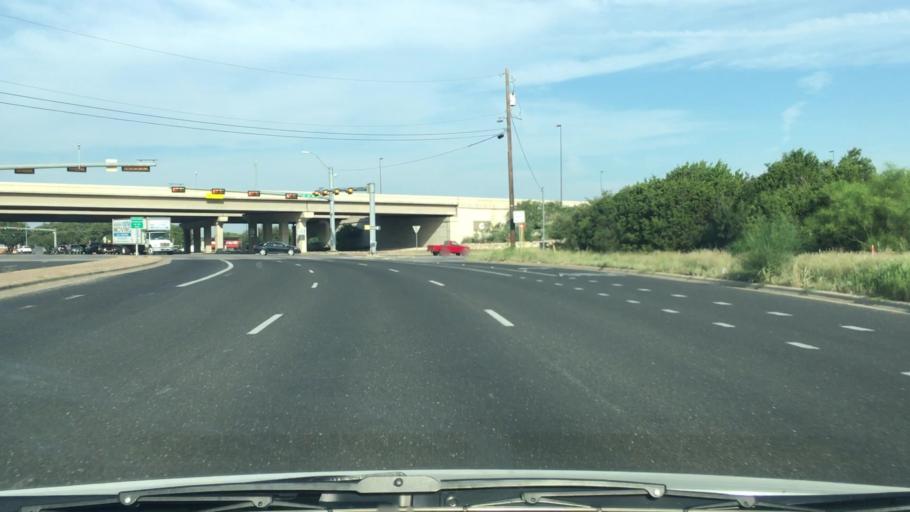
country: US
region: Texas
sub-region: Williamson County
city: Anderson Mill
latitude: 30.4804
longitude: -97.8011
